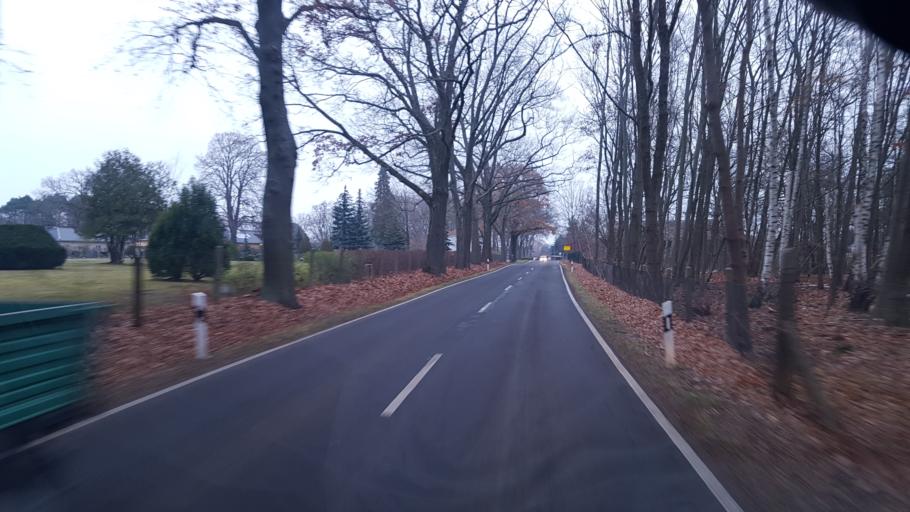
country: DE
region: Brandenburg
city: Drachhausen
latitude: 51.8888
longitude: 14.3088
